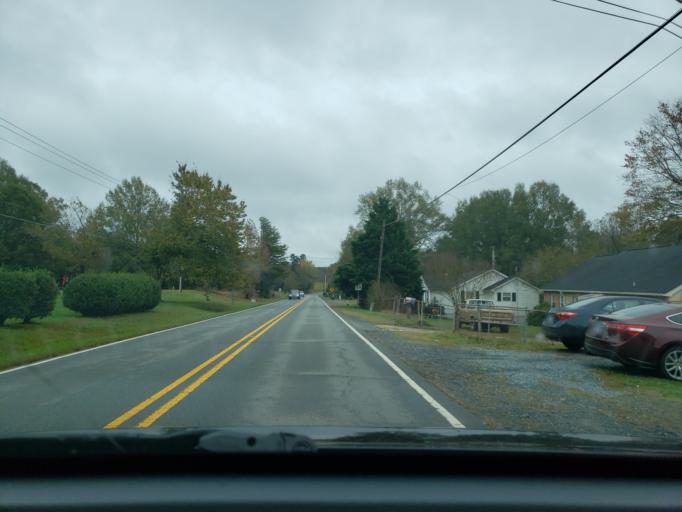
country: US
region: North Carolina
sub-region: Stokes County
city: Walnut Cove
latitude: 36.3182
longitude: -80.1411
